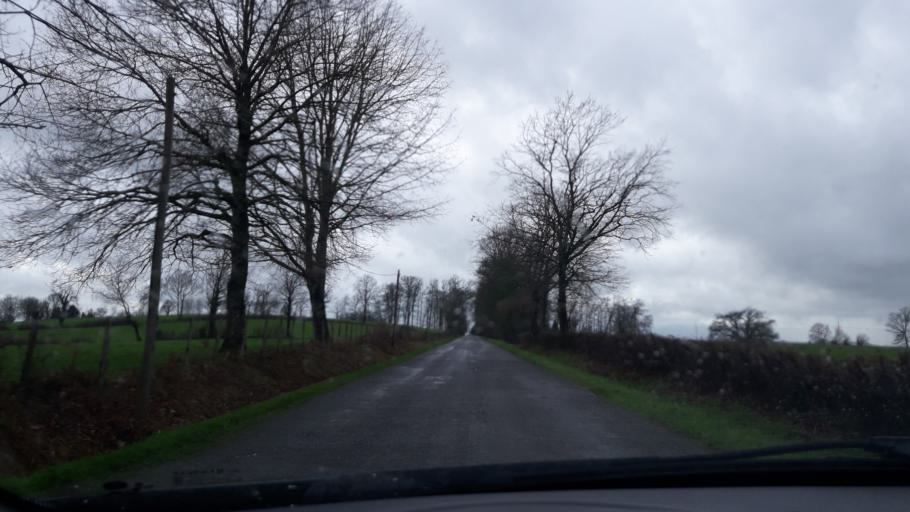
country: FR
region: Limousin
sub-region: Departement de la Haute-Vienne
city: Saint-Paul
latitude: 45.7512
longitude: 1.4128
